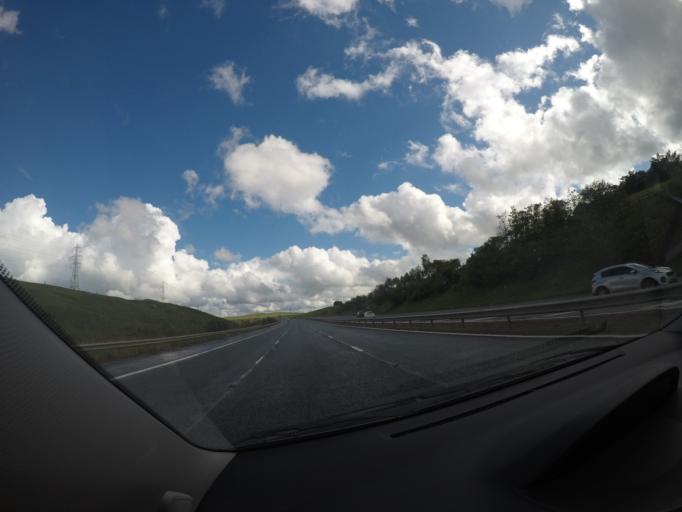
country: GB
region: Scotland
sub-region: South Lanarkshire
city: Douglas
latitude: 55.5534
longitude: -3.8010
